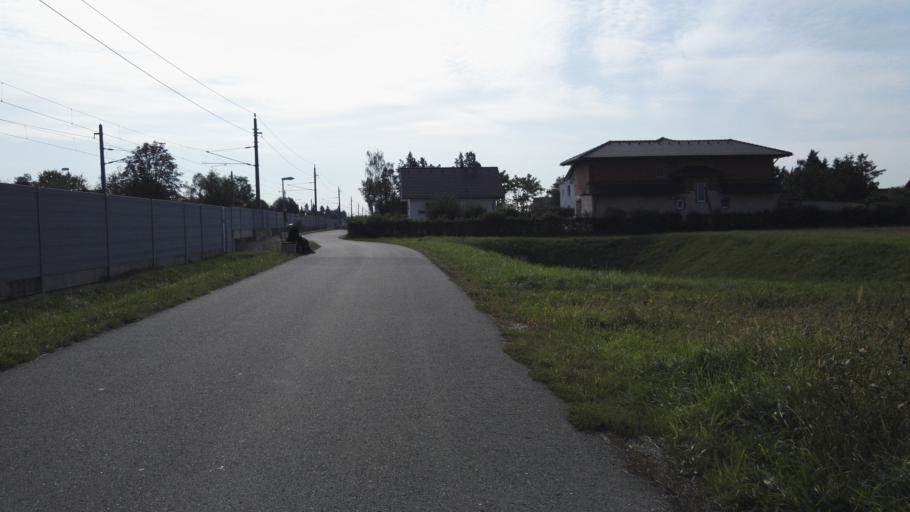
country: AT
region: Styria
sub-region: Politischer Bezirk Graz-Umgebung
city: Feldkirchen bei Graz
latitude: 46.9944
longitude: 15.4514
